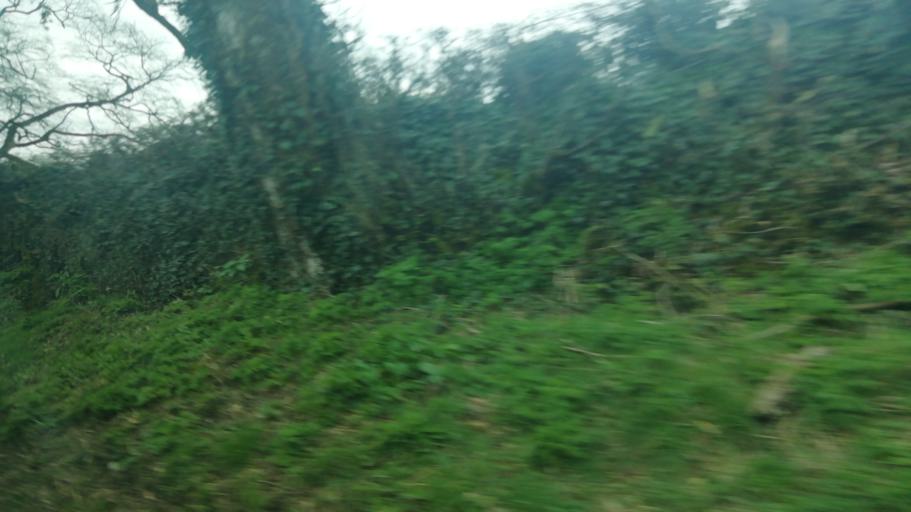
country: IE
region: Leinster
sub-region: Kildare
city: Derrinturn
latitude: 53.3489
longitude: -6.9564
